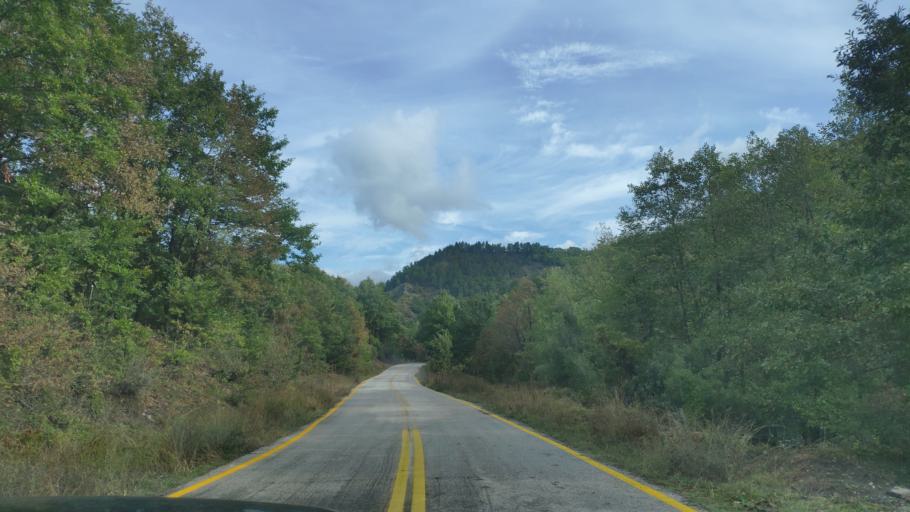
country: GR
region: West Macedonia
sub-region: Nomos Kastorias
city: Nestorio
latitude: 40.2343
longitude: 20.9892
